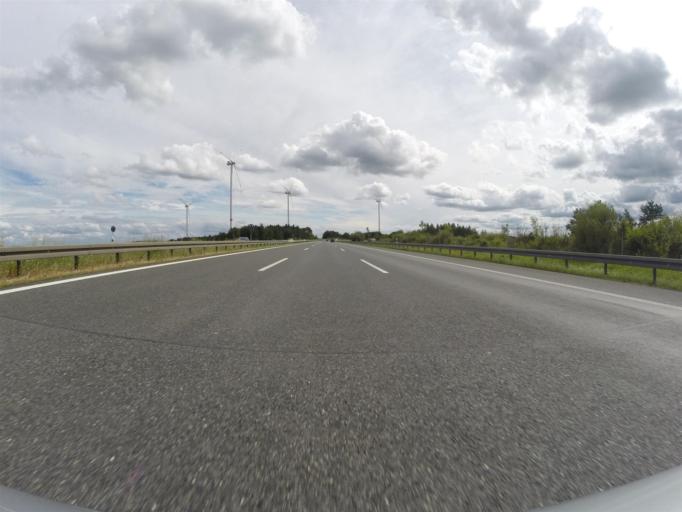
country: DE
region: Bavaria
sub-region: Upper Franconia
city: Pegnitz
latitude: 49.8134
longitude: 11.4987
